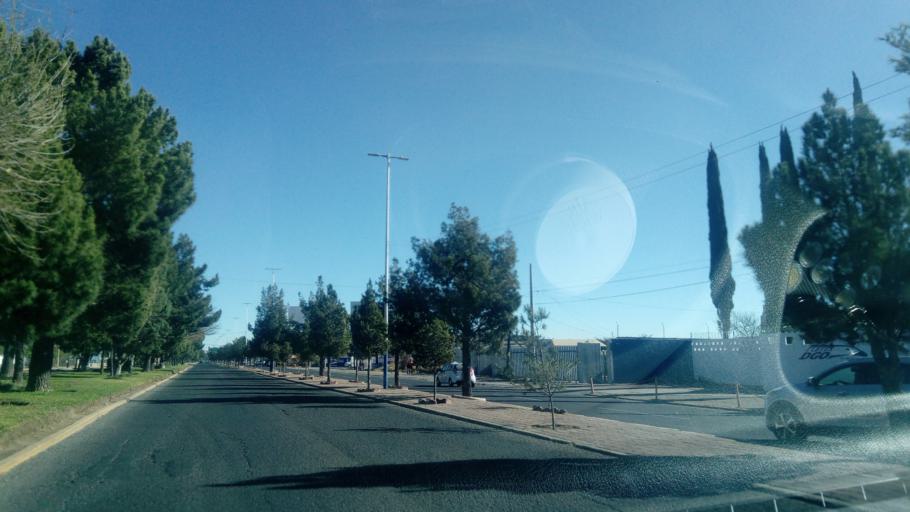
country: MX
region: Durango
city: Victoria de Durango
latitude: 24.0587
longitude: -104.6106
